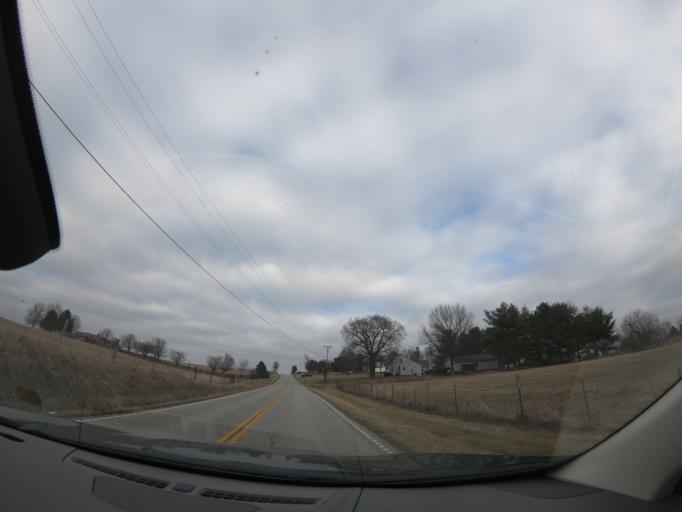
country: US
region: Kentucky
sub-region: Nelson County
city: Bardstown
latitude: 37.8521
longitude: -85.3484
